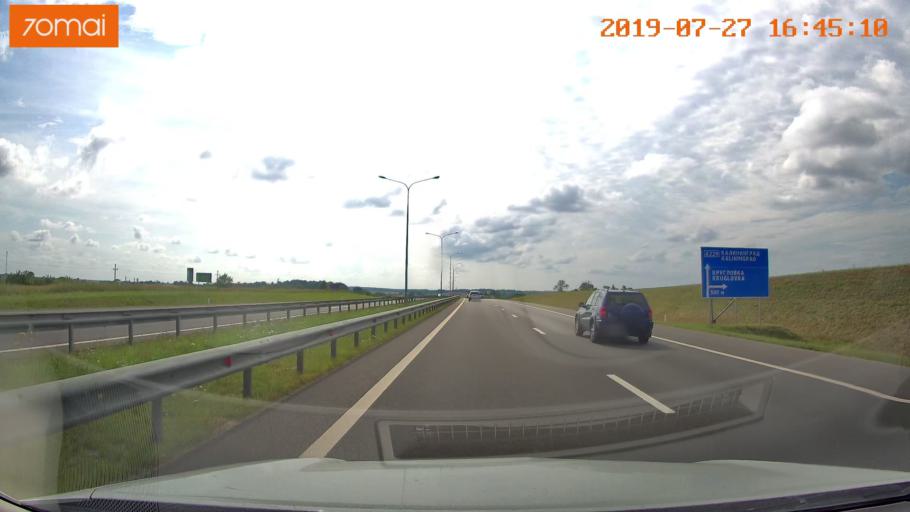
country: RU
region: Kaliningrad
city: Gvardeysk
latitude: 54.6712
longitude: 21.0565
